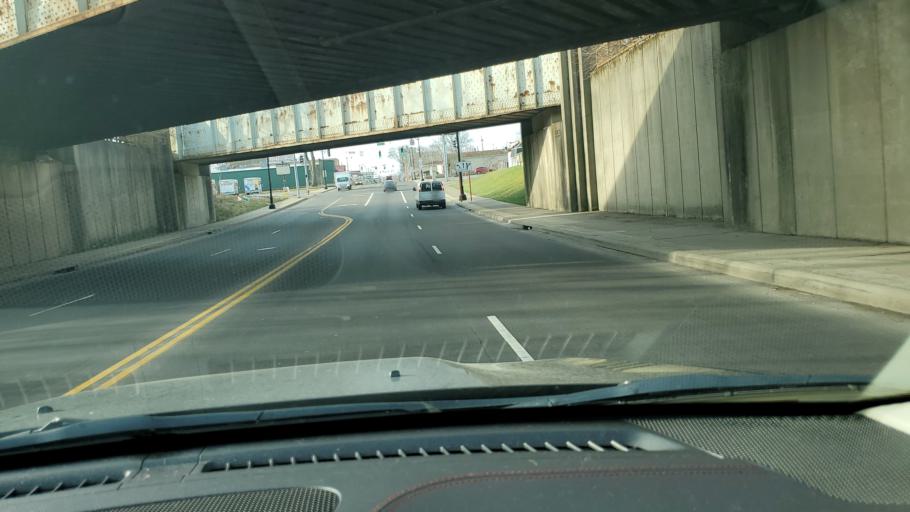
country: US
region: Ohio
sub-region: Trumbull County
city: Niles
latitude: 41.1850
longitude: -80.7649
